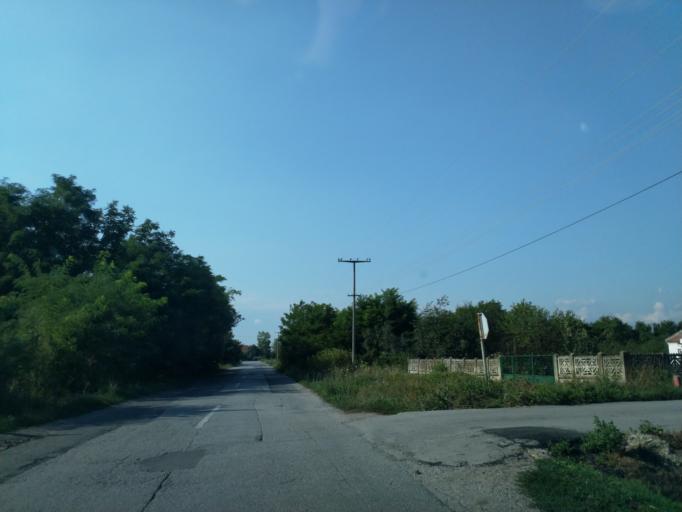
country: RS
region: Central Serbia
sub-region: Rasinski Okrug
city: Cicevac
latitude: 43.7675
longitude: 21.4282
